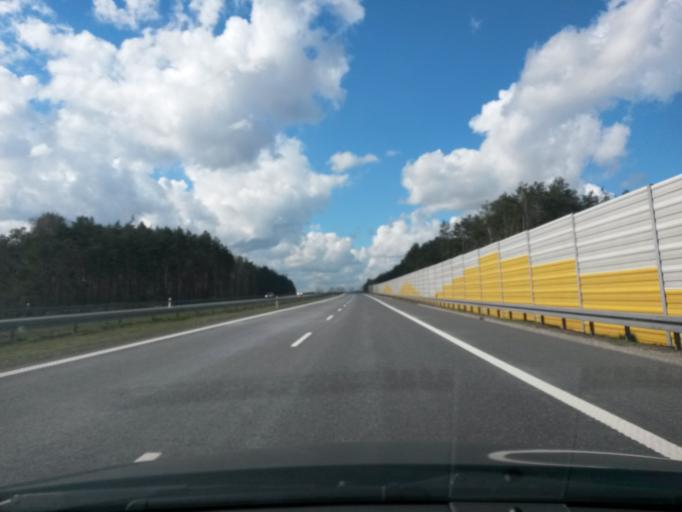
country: PL
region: Lodz Voivodeship
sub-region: Powiat leczycki
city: Swinice Warckie
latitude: 52.0239
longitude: 18.9233
